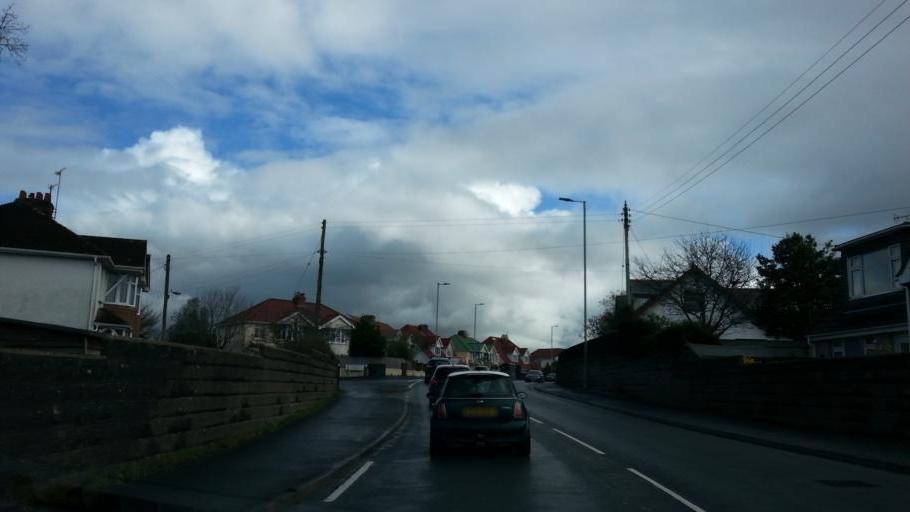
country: GB
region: England
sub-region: Devon
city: Barnstaple
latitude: 51.0718
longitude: -4.0791
